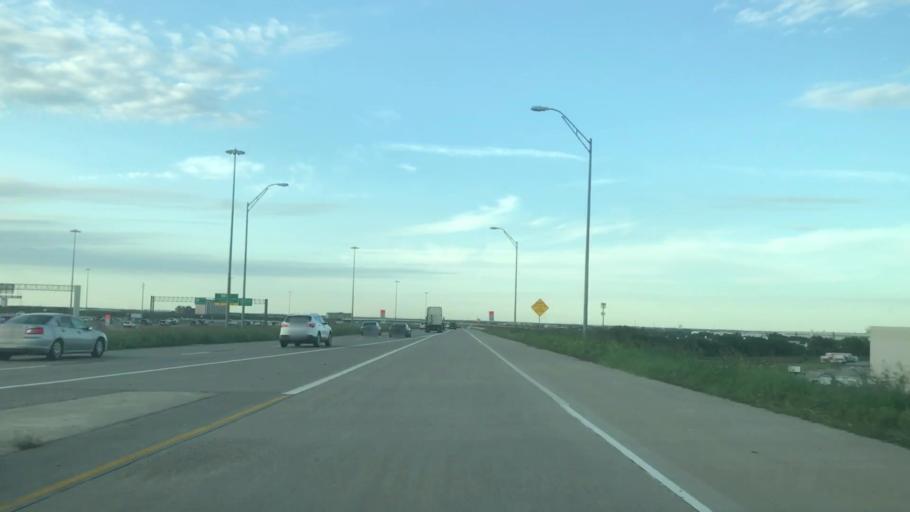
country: US
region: Texas
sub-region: Dallas County
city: Coppell
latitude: 32.9392
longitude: -97.0391
